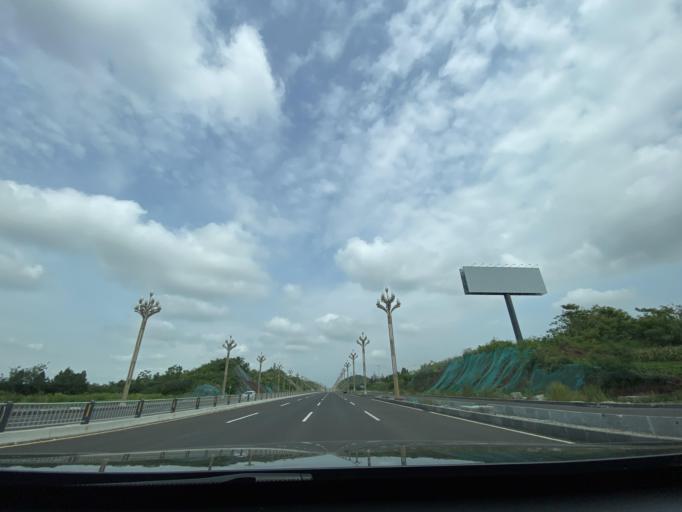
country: CN
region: Sichuan
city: Jiancheng
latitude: 30.3887
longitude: 104.6193
